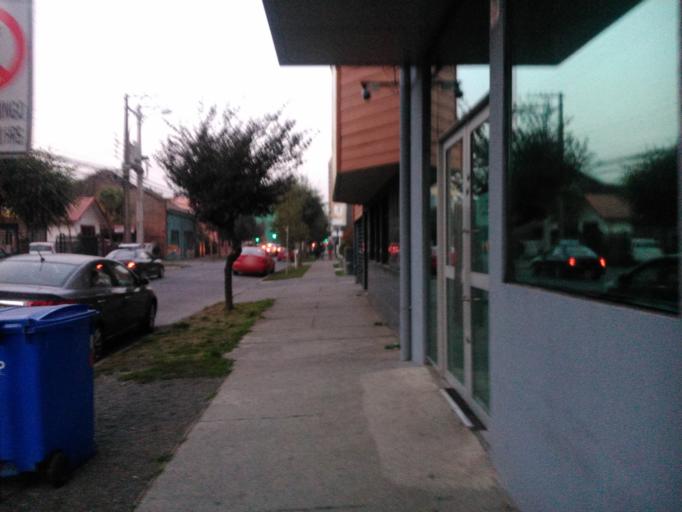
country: CL
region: Araucania
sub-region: Provincia de Cautin
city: Temuco
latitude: -38.7409
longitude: -72.5950
